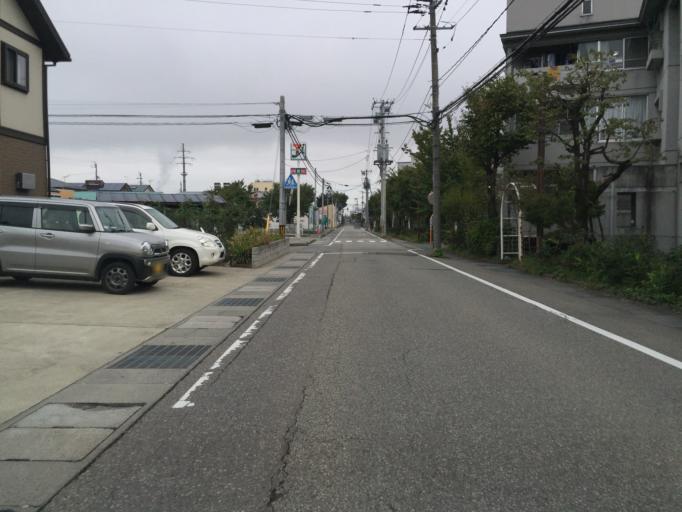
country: JP
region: Fukushima
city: Kitakata
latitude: 37.4761
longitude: 139.9114
